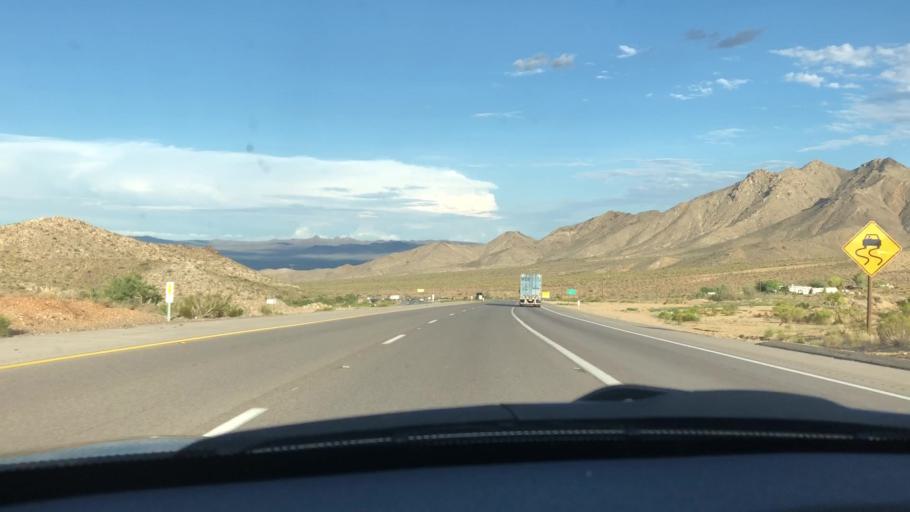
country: US
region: Nevada
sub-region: Clark County
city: Sandy Valley
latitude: 35.4635
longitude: -115.4806
